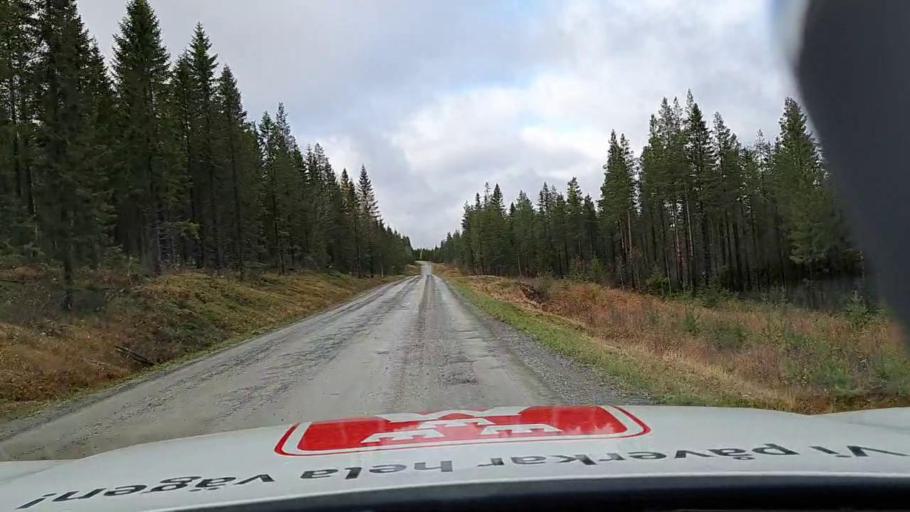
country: SE
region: Jaemtland
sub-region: Bergs Kommun
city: Hoverberg
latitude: 63.0087
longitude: 14.1196
